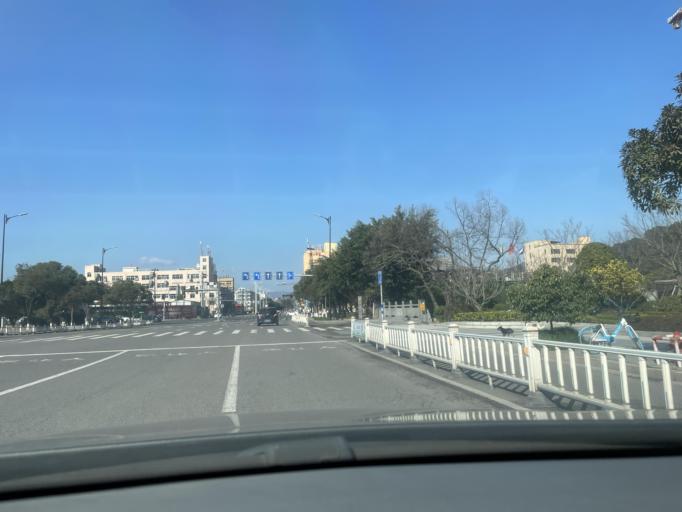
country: CN
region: Zhejiang Sheng
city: Shuangyu
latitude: 27.9915
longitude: 120.6116
